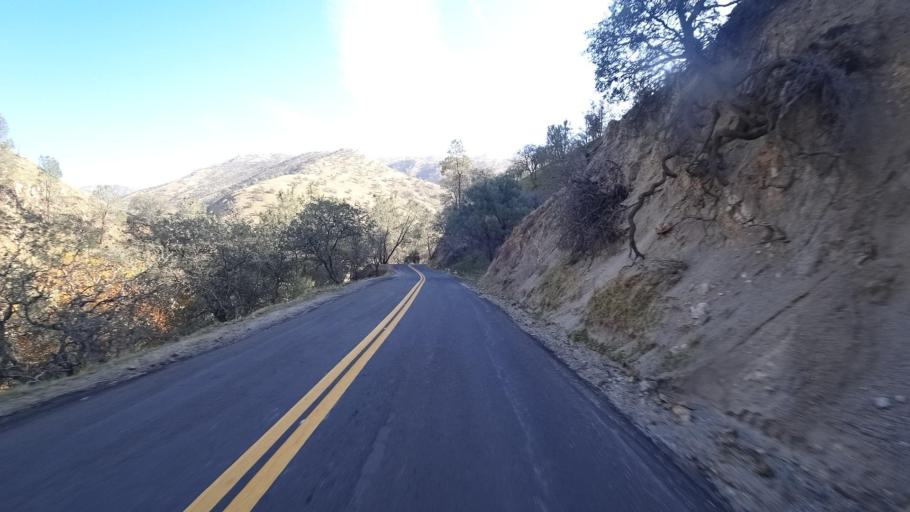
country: US
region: California
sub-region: Kern County
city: Bear Valley Springs
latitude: 35.3091
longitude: -118.5862
